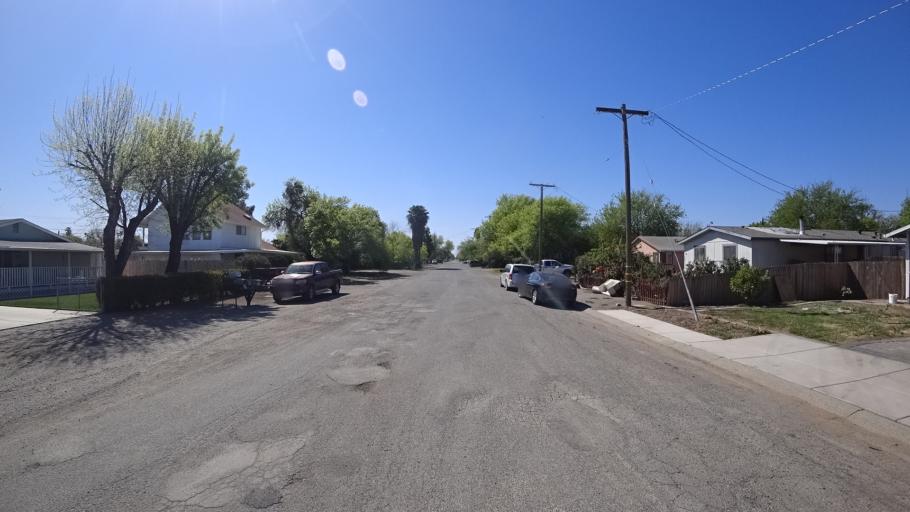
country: US
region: California
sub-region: Glenn County
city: Willows
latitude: 39.5287
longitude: -122.1895
